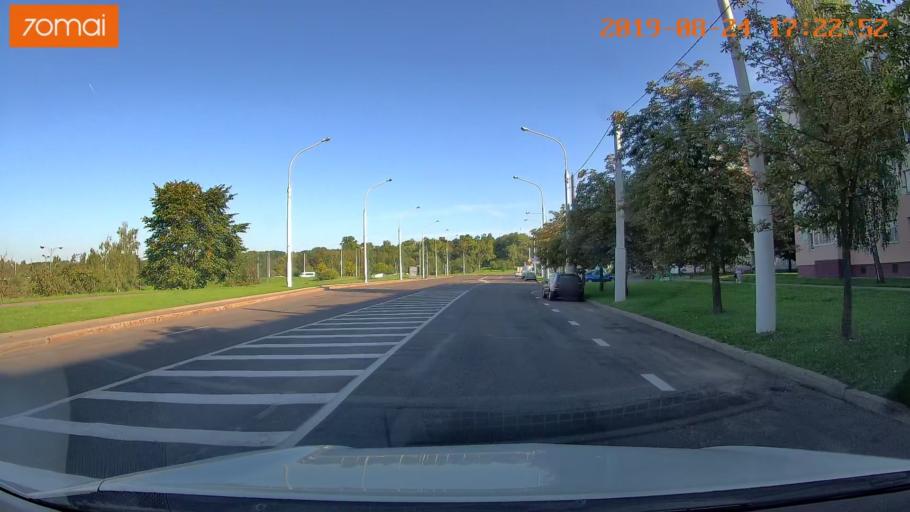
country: BY
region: Minsk
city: Hatava
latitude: 53.8437
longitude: 27.6487
